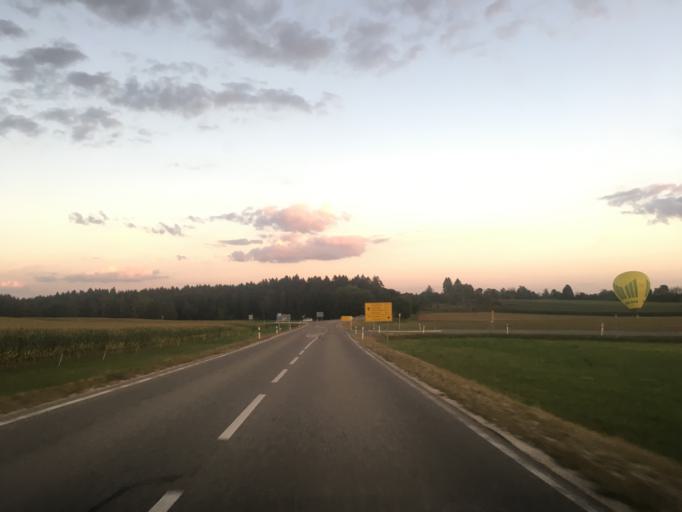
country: DE
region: Baden-Wuerttemberg
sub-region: Tuebingen Region
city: Hayingen
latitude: 48.2986
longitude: 9.4546
